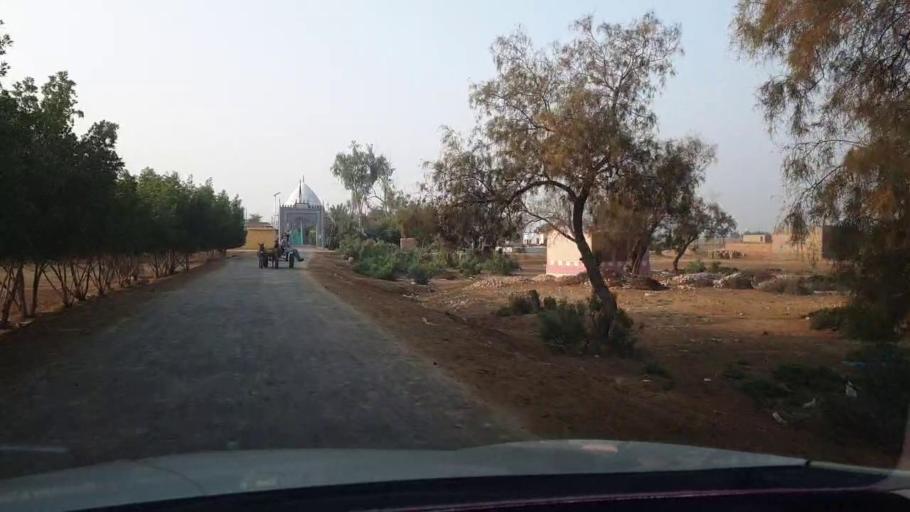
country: PK
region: Sindh
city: Sehwan
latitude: 26.3547
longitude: 67.7623
